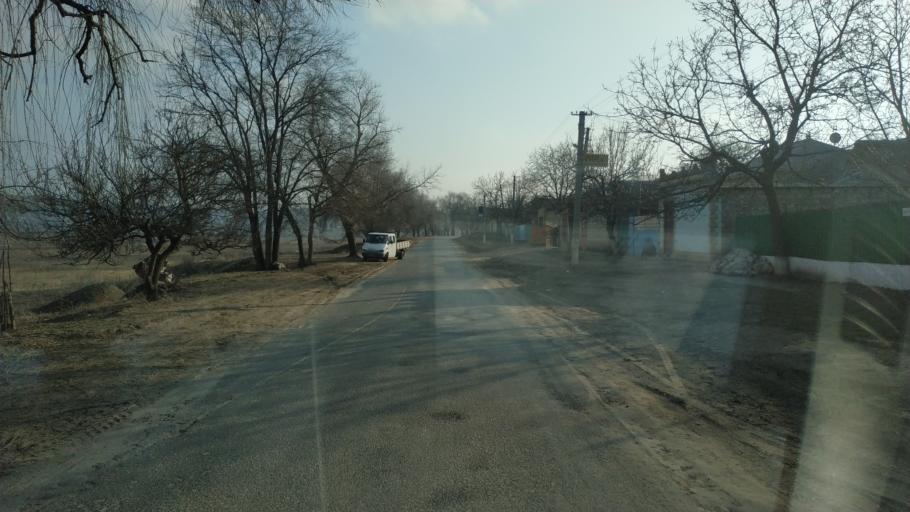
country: MD
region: Hincesti
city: Dancu
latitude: 46.7726
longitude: 28.3463
